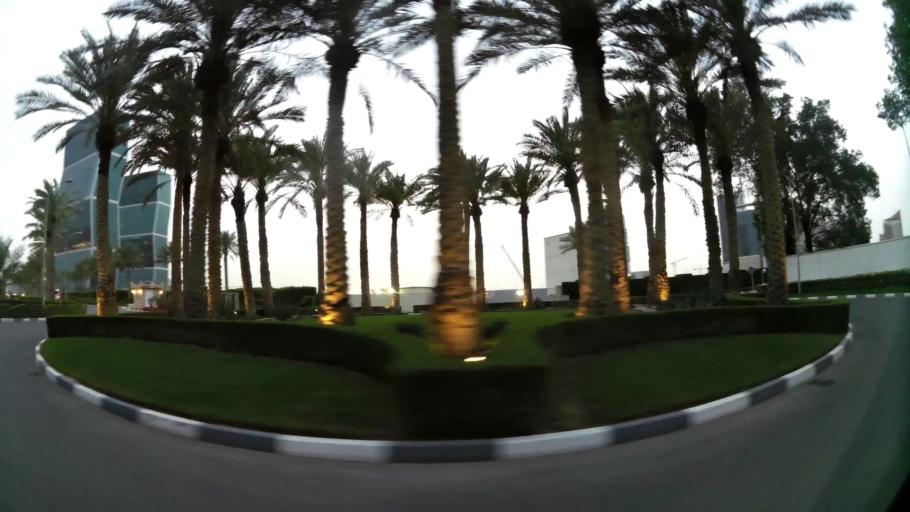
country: QA
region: Baladiyat ad Dawhah
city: Doha
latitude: 25.3802
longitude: 51.5287
